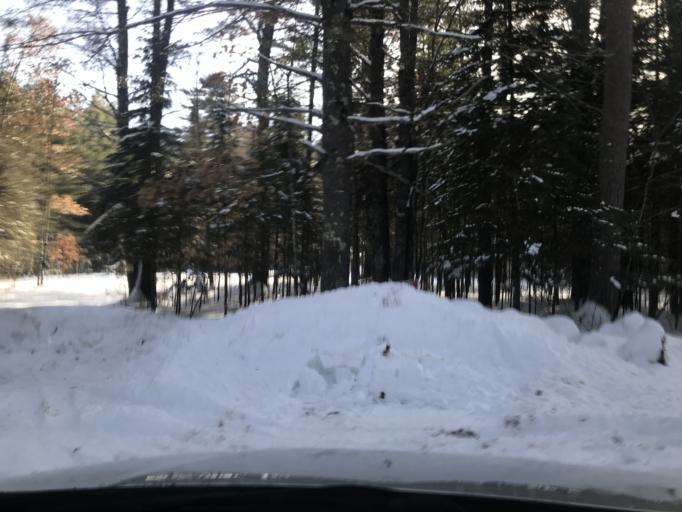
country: US
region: Wisconsin
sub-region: Menominee County
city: Legend Lake
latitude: 45.3422
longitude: -88.4592
